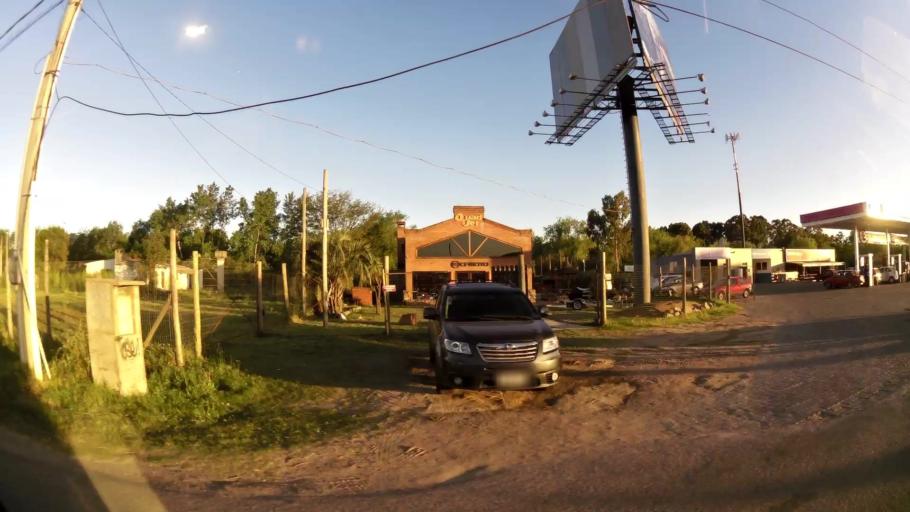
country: UY
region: Canelones
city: Barra de Carrasco
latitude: -34.8428
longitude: -56.0146
